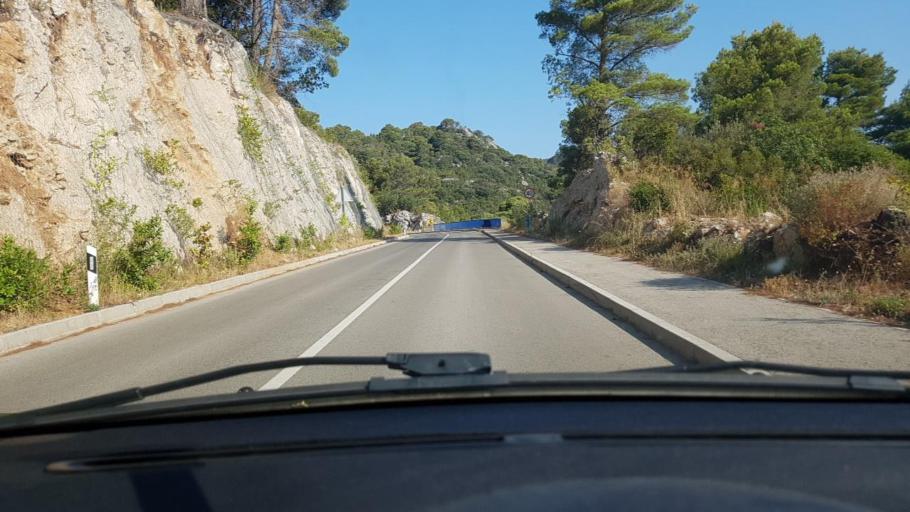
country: HR
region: Dubrovacko-Neretvanska
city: Blato
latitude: 42.7851
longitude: 17.3770
